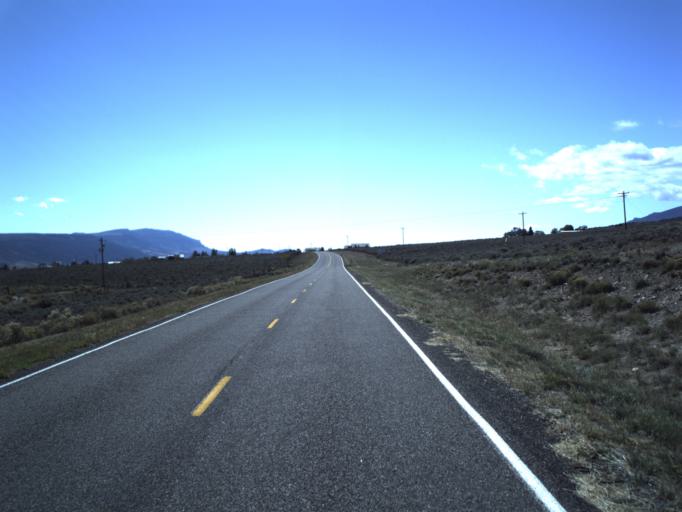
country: US
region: Utah
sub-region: Sevier County
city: Monroe
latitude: 38.5284
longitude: -111.8797
